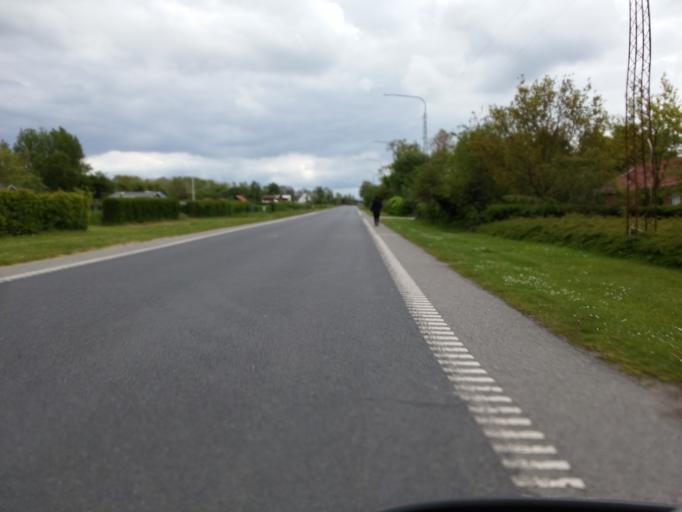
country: DK
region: South Denmark
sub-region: Kerteminde Kommune
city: Munkebo
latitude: 55.4636
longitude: 10.5450
